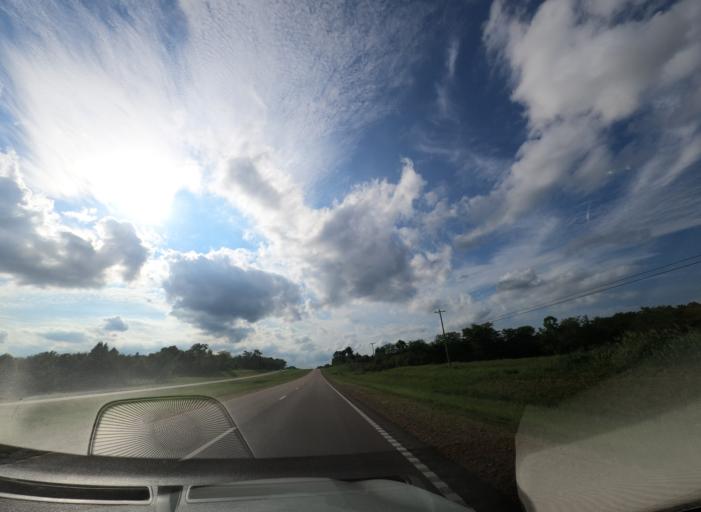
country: US
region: Tennessee
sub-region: Fayette County
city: Piperton
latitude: 34.9756
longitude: -89.5687
